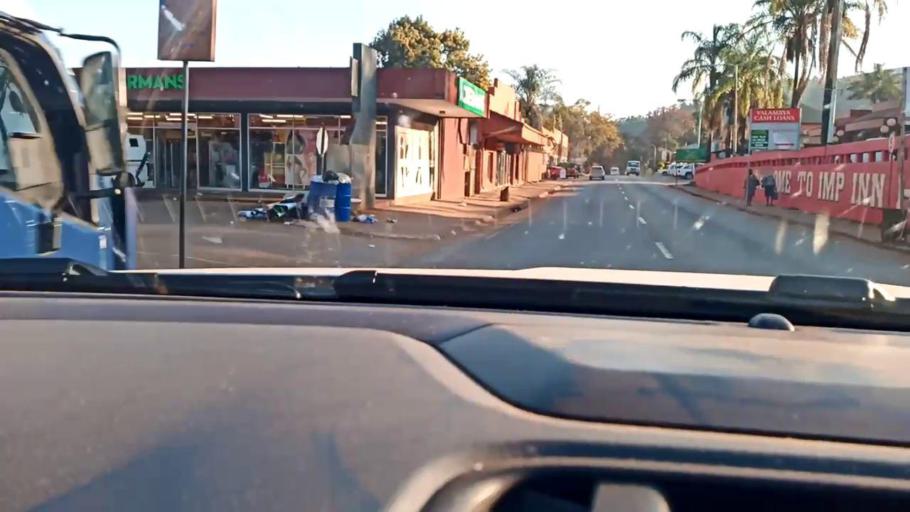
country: ZA
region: Limpopo
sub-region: Mopani District Municipality
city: Duiwelskloof
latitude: -23.6972
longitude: 30.1392
